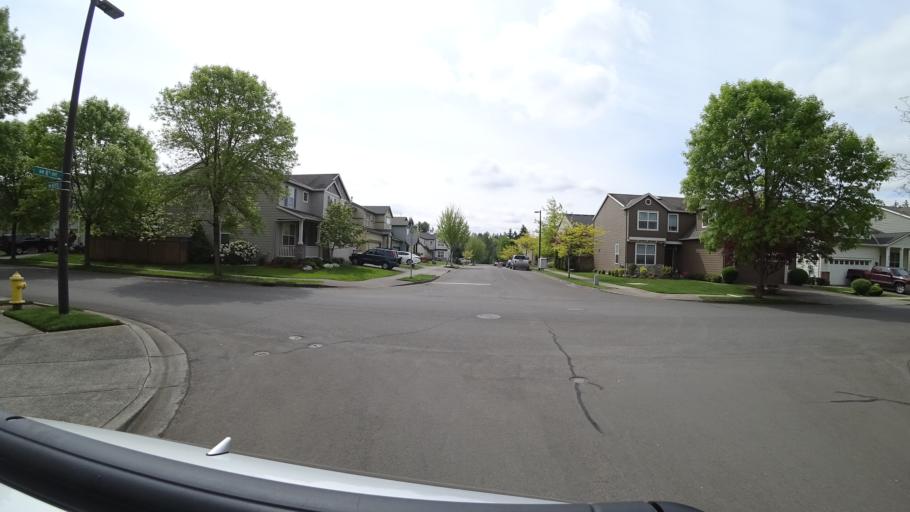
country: US
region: Oregon
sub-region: Washington County
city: Hillsboro
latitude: 45.5365
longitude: -122.9978
